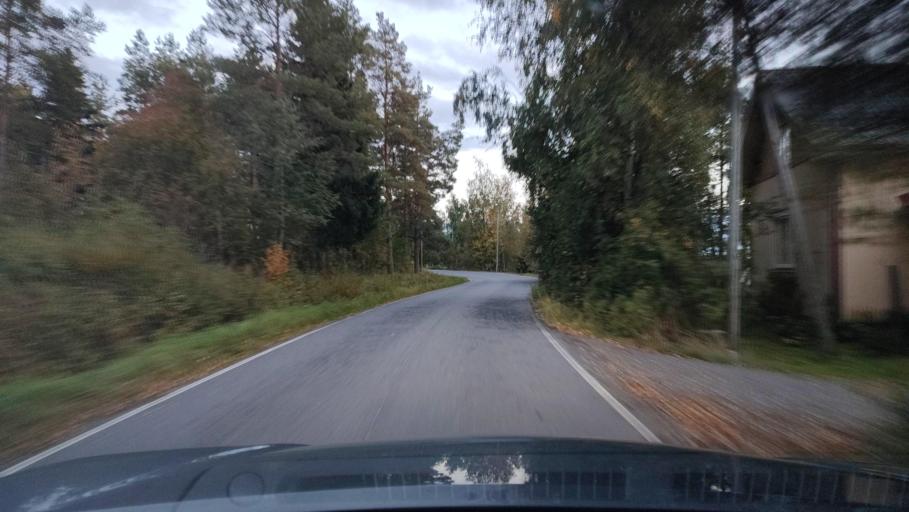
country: FI
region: Ostrobothnia
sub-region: Sydosterbotten
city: Kristinestad
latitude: 62.2652
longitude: 21.5265
